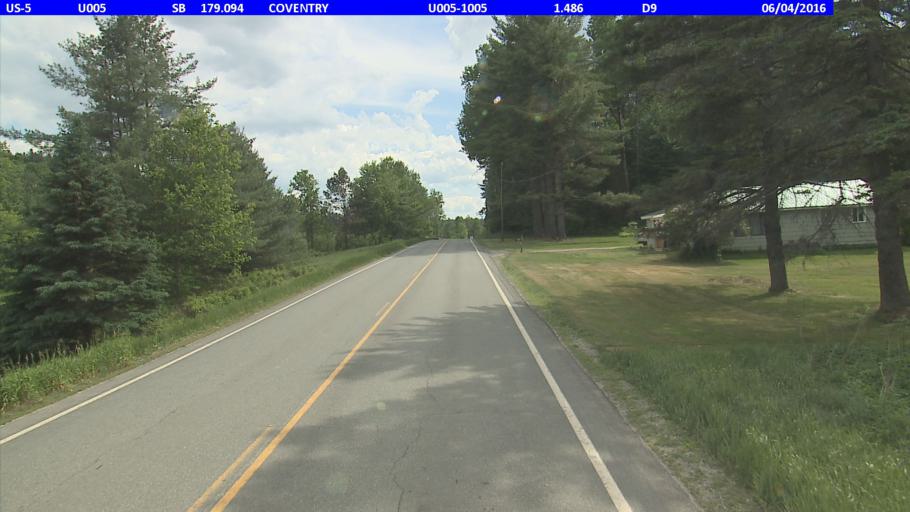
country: US
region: Vermont
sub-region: Orleans County
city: Newport
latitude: 44.8777
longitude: -72.2524
